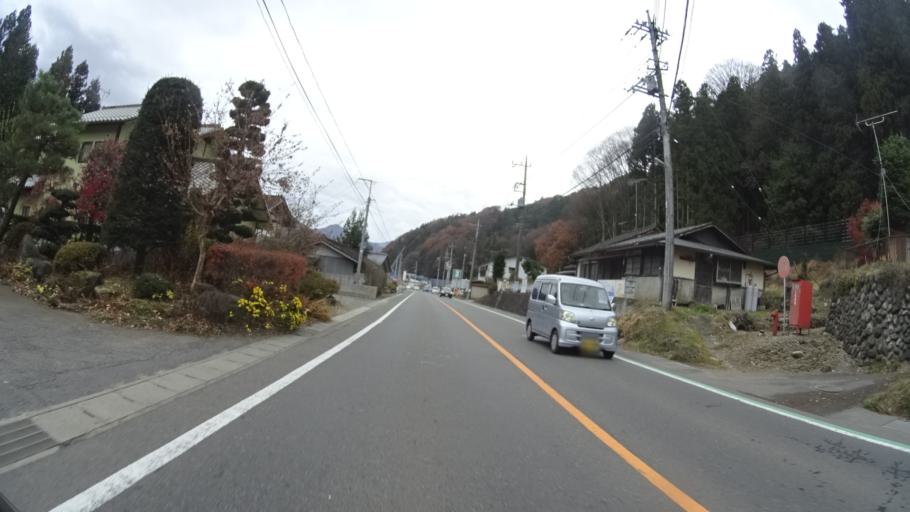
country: JP
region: Gunma
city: Numata
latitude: 36.6905
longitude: 139.2078
